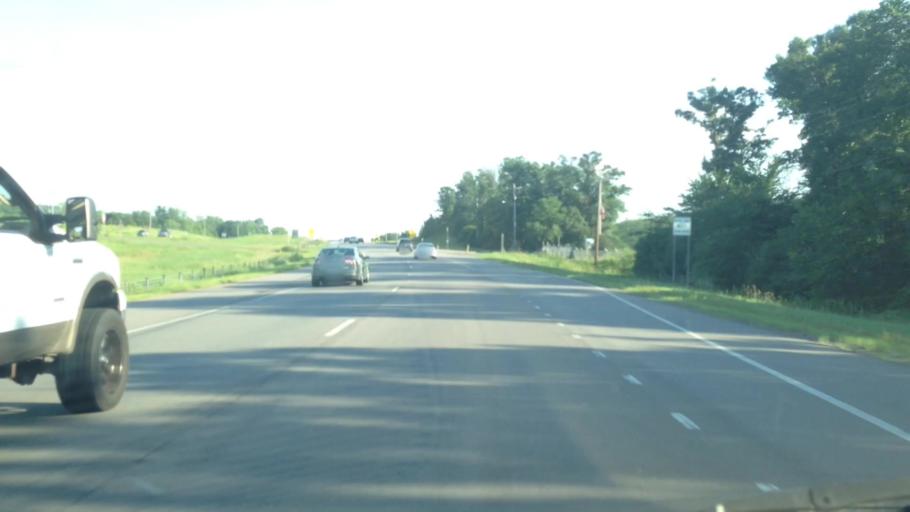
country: US
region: Minnesota
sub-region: Sherburne County
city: Zimmerman
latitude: 45.3798
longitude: -93.5644
